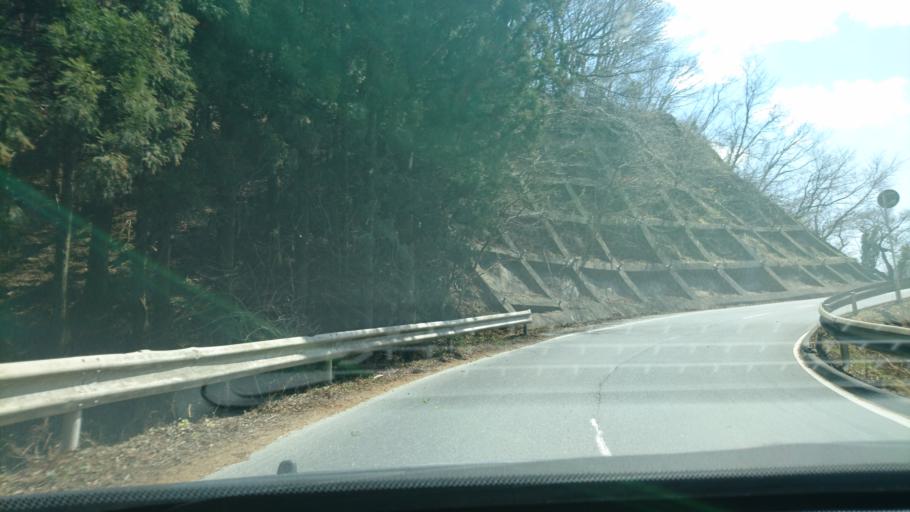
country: JP
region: Miyagi
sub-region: Oshika Gun
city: Onagawa Cho
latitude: 38.4425
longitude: 141.4654
